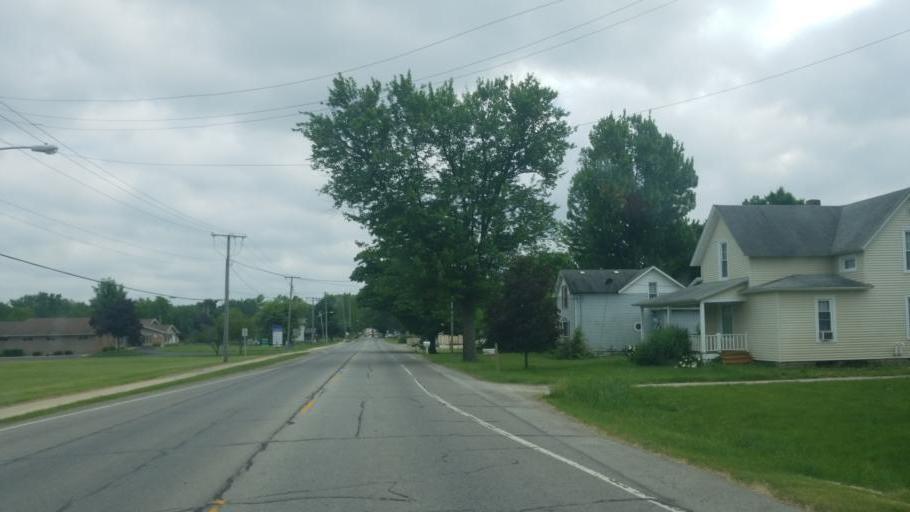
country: US
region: Indiana
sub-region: Elkhart County
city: Nappanee
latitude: 41.4519
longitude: -86.0014
